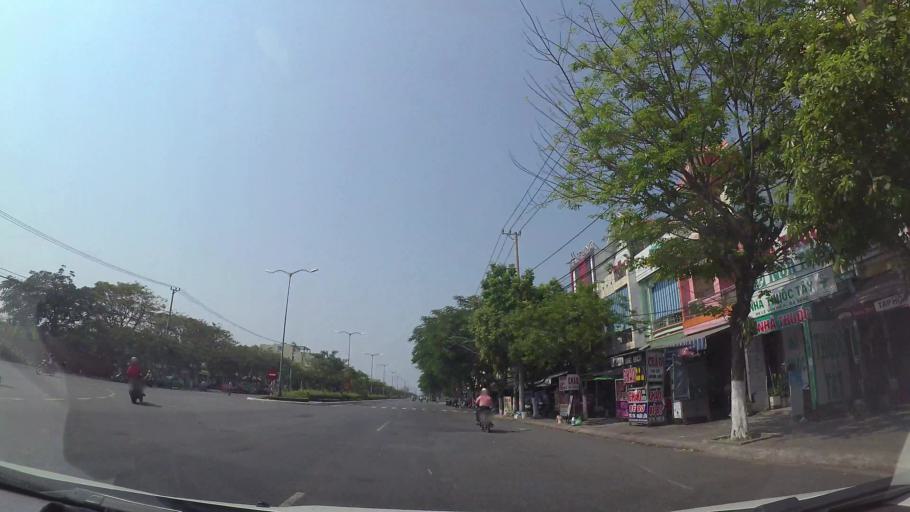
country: VN
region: Da Nang
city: Ngu Hanh Son
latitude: 16.0234
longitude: 108.2507
